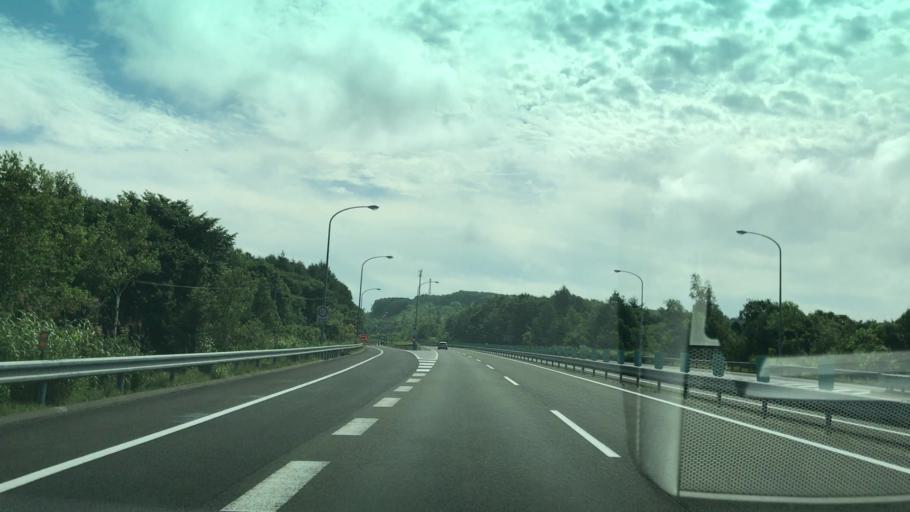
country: JP
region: Hokkaido
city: Chitose
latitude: 42.8778
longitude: 141.7298
